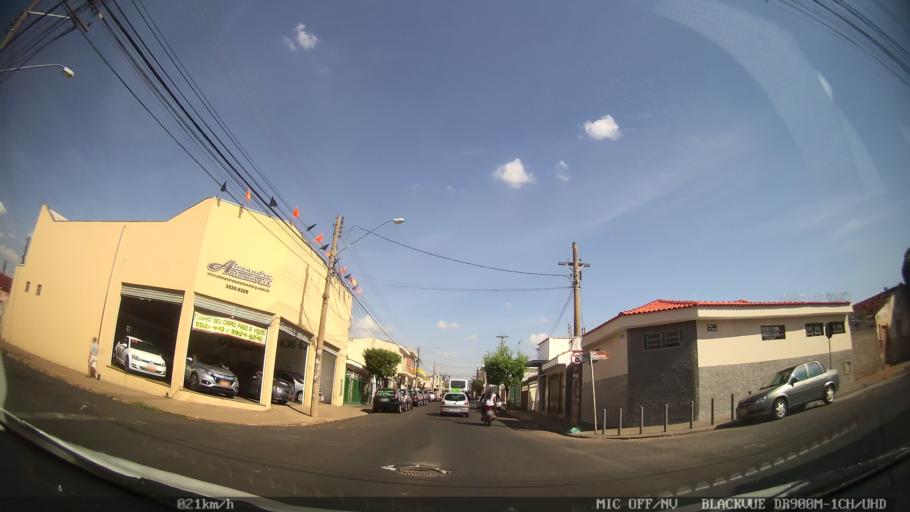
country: BR
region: Sao Paulo
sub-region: Ribeirao Preto
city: Ribeirao Preto
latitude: -21.1854
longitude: -47.8265
